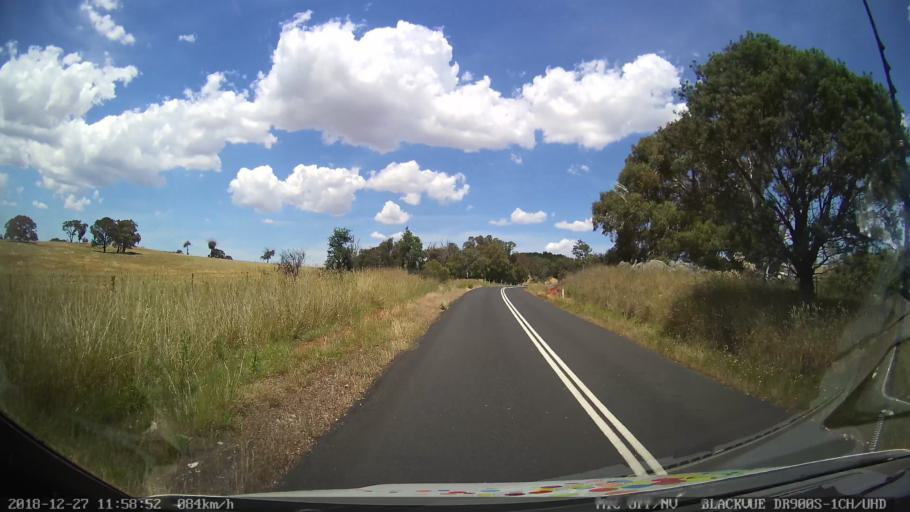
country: AU
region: New South Wales
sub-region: Blayney
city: Blayney
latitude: -33.7293
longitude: 149.3819
